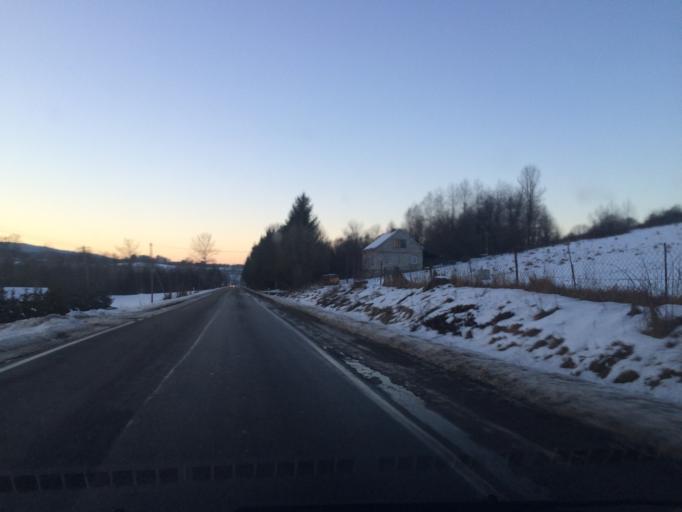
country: PL
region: Subcarpathian Voivodeship
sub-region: Powiat bieszczadzki
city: Czarna
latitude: 49.3698
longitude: 22.6535
